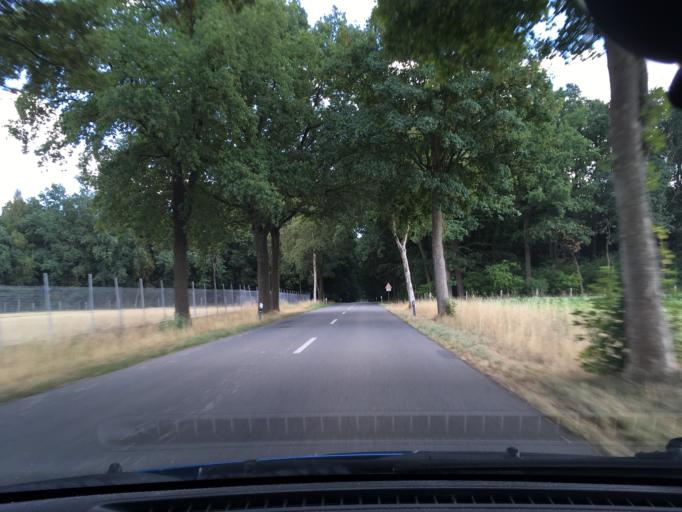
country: DE
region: Lower Saxony
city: Wriedel
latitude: 53.0489
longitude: 10.2556
